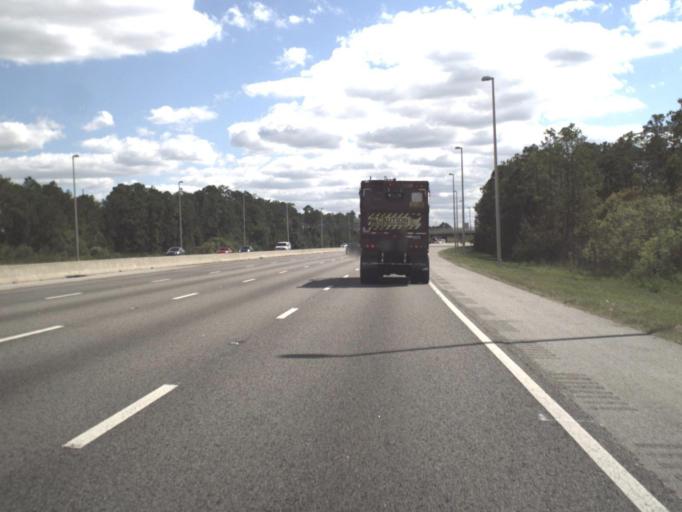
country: US
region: Florida
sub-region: Orange County
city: Oak Ridge
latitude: 28.4547
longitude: -81.4252
